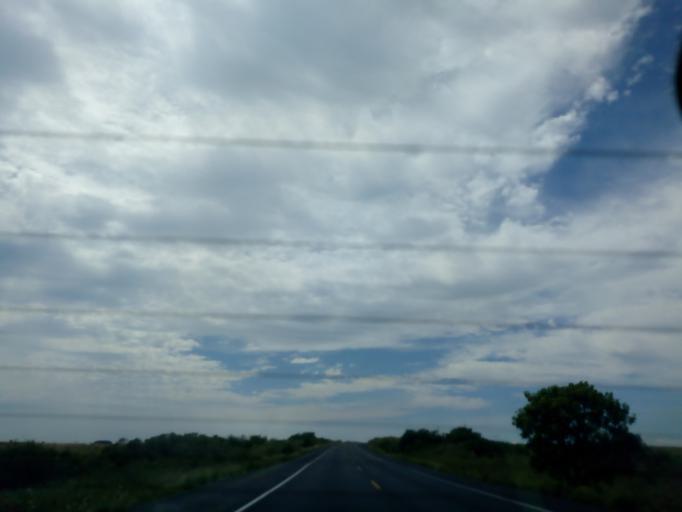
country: BR
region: Rio Grande do Sul
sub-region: Quarai
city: Quarai
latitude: -29.9738
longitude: -56.5546
